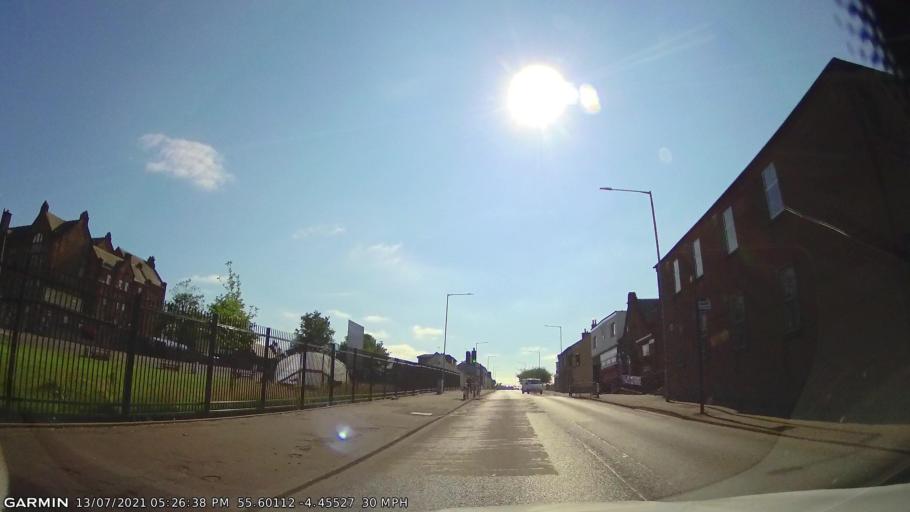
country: GB
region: Scotland
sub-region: East Ayrshire
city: Kilmarnock
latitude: 55.6012
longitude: -4.4551
